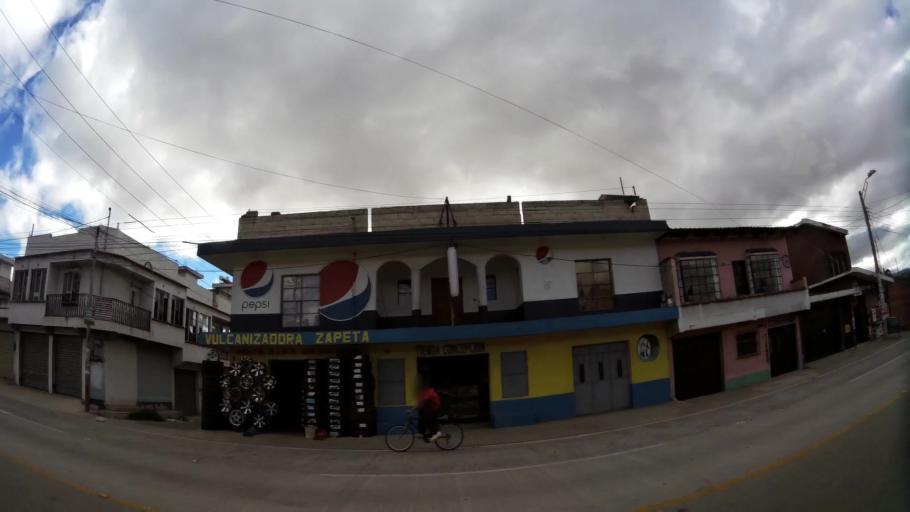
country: GT
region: Quetzaltenango
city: Salcaja
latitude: 14.8723
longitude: -91.4650
